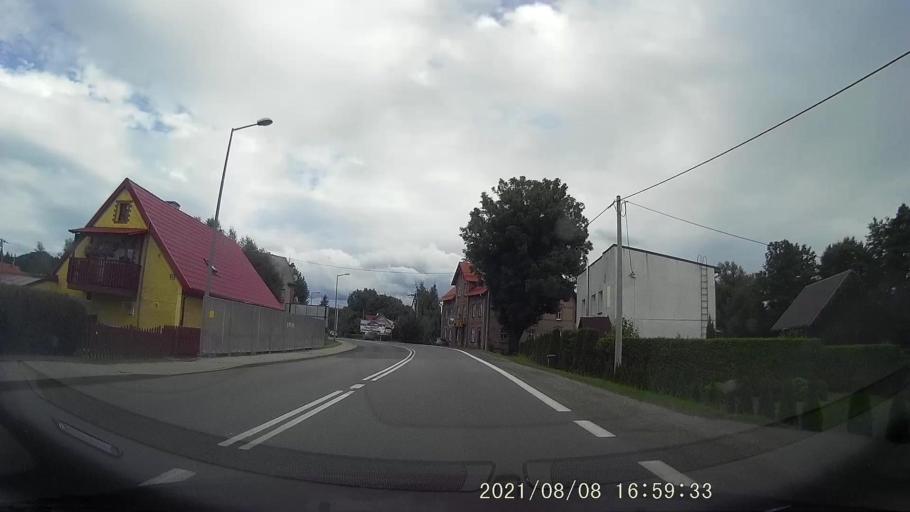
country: PL
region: Lower Silesian Voivodeship
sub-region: Powiat klodzki
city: Kudowa-Zdroj
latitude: 50.4270
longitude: 16.2516
